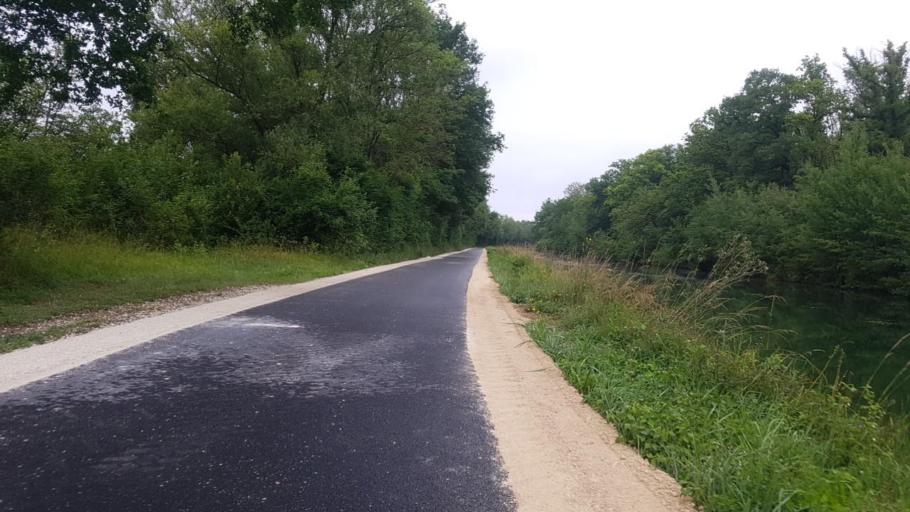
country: FR
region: Champagne-Ardenne
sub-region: Departement de la Marne
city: Vitry-le-Francois
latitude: 48.7976
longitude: 4.5262
